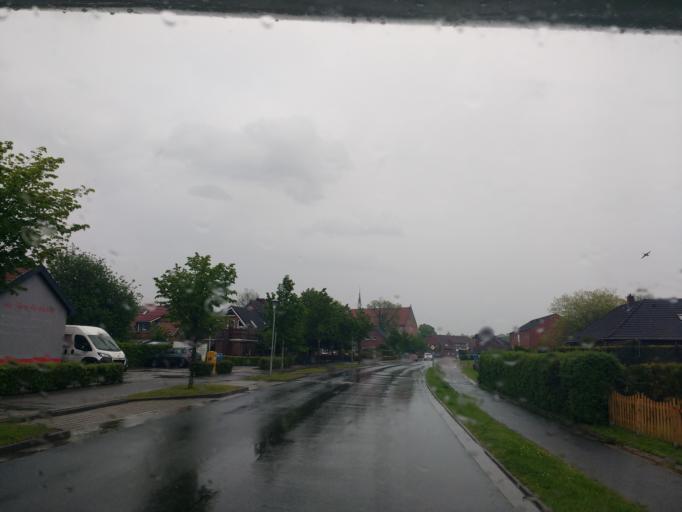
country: DE
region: Lower Saxony
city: Jever
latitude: 53.6646
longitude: 7.9139
